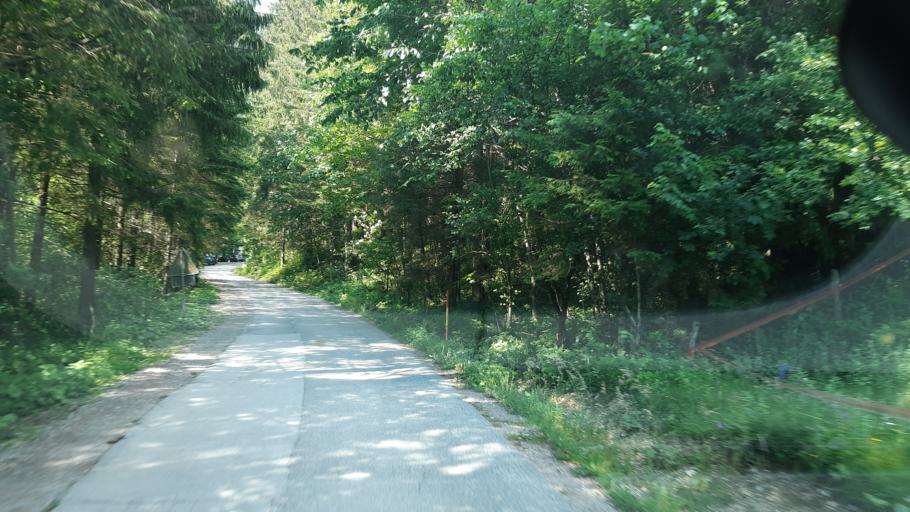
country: SI
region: Radovljica
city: Radovljica
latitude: 46.3934
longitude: 14.2181
